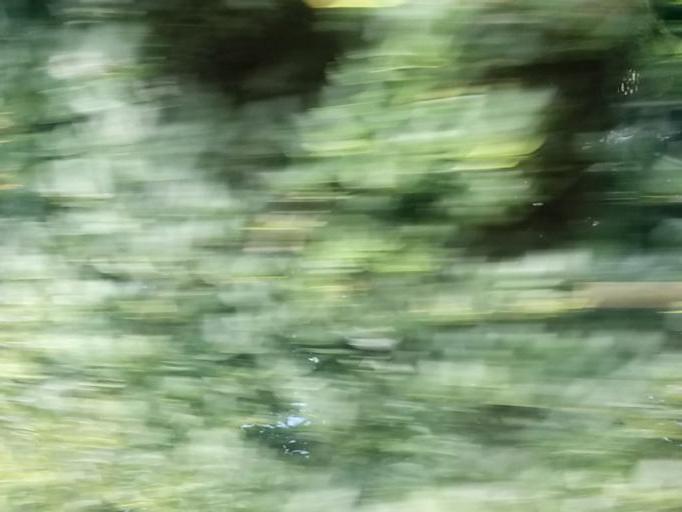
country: JP
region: Nara
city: Nara-shi
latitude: 34.6679
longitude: 135.7835
